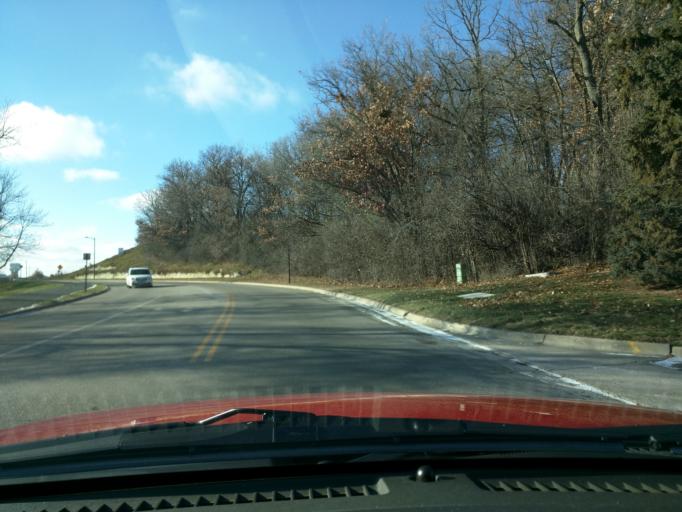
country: US
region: Minnesota
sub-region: Hennepin County
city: Eden Prairie
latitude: 44.8665
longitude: -93.4149
